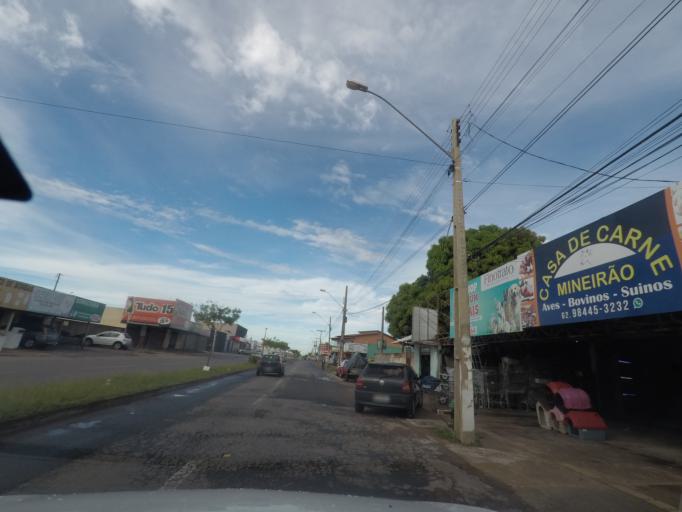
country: BR
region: Goias
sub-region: Aparecida De Goiania
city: Aparecida de Goiania
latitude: -16.7814
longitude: -49.3572
